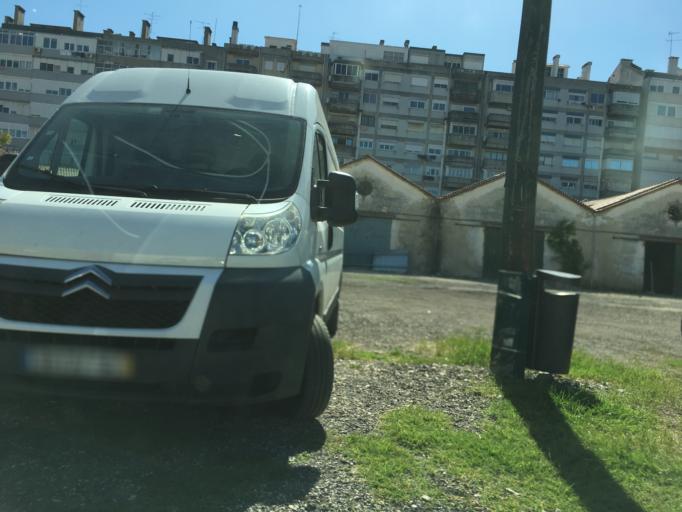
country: PT
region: Lisbon
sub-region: Odivelas
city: Pontinha
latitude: 38.7460
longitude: -9.1867
